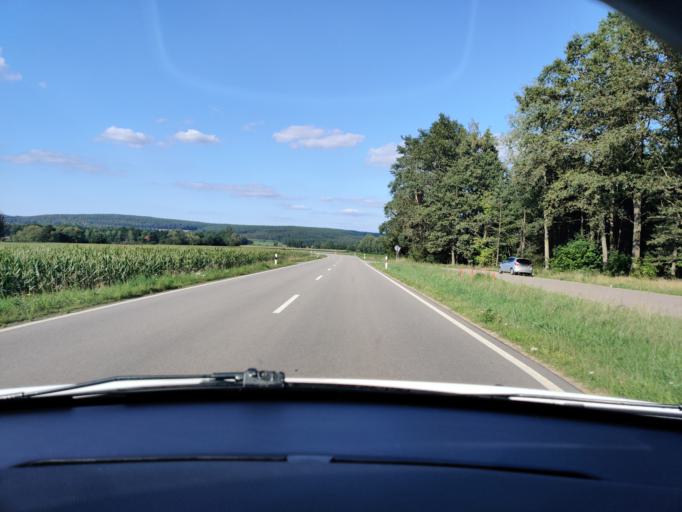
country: DE
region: Bavaria
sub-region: Upper Palatinate
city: Schwarzenfeld
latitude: 49.3625
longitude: 12.1540
